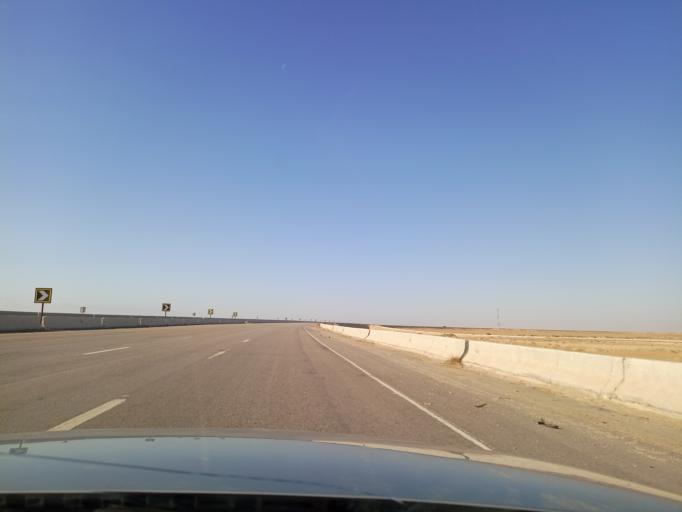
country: EG
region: Muhafazat al Fayyum
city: Tamiyah
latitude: 29.5663
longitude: 30.8335
